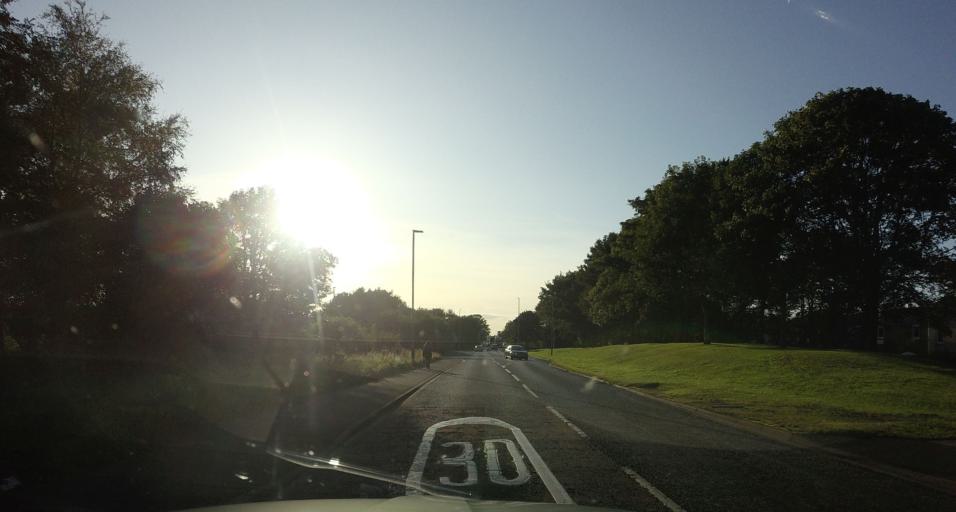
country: GB
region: Scotland
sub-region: Aberdeenshire
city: Westhill
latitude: 57.1492
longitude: -2.2897
